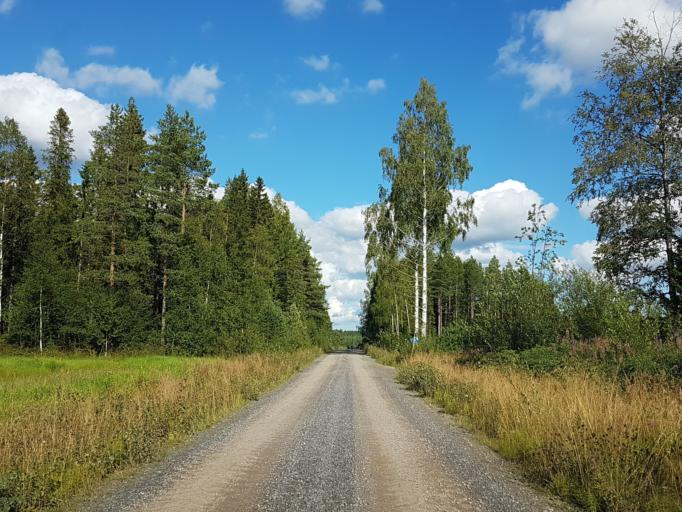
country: SE
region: Vaesterbotten
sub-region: Skelleftea Kommun
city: Burtraesk
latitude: 64.2934
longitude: 20.4672
